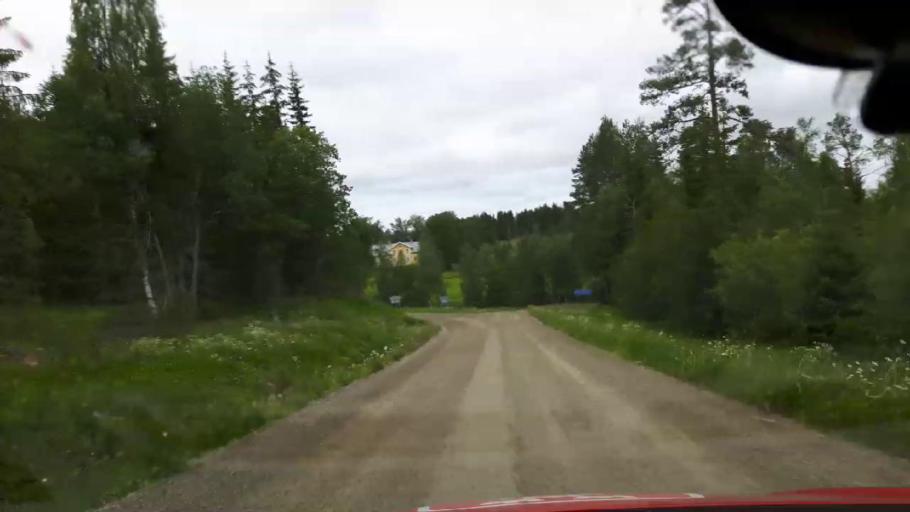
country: SE
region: Jaemtland
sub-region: OEstersunds Kommun
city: Brunflo
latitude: 62.9449
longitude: 14.9845
